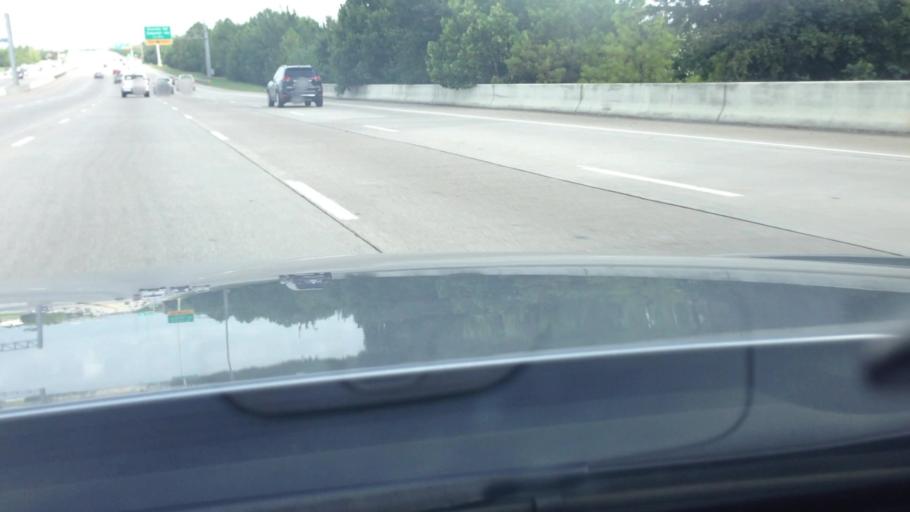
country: US
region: Texas
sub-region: Harris County
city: Hudson
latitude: 29.9466
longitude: -95.5284
